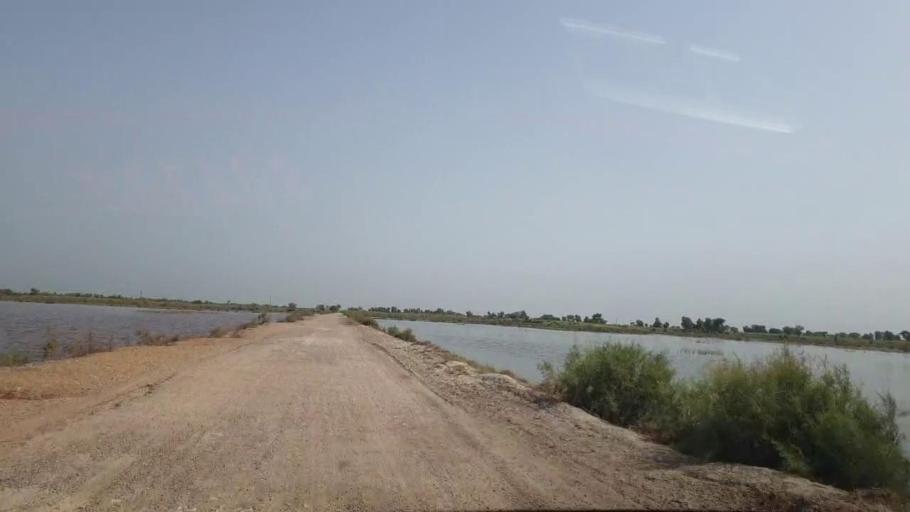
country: PK
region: Sindh
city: Sakrand
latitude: 26.3010
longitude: 68.2202
